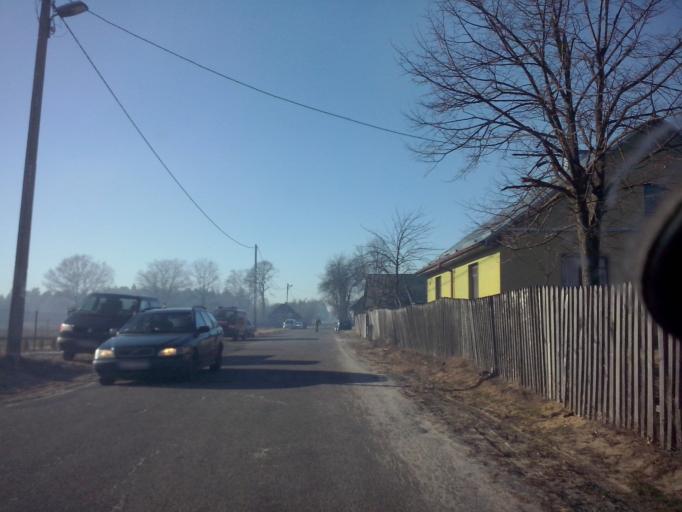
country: PL
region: Subcarpathian Voivodeship
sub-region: Powiat nizanski
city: Harasiuki
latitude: 50.4720
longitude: 22.5237
